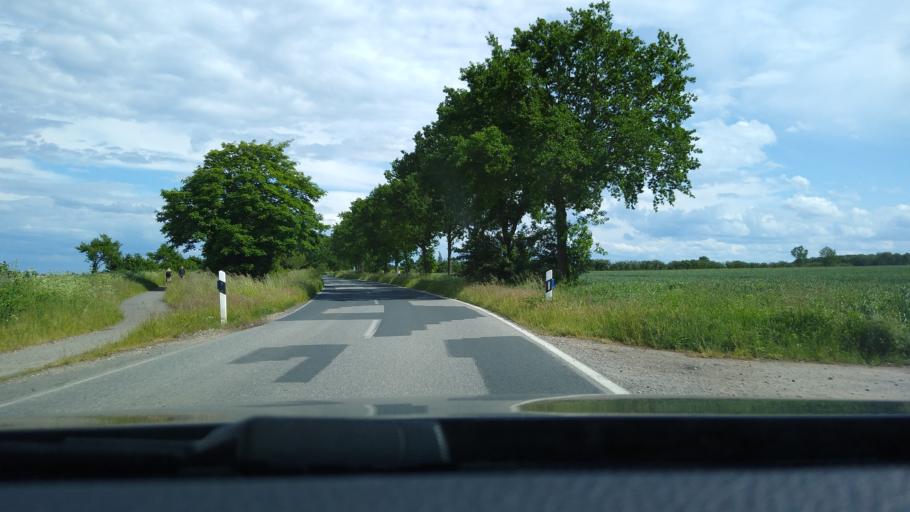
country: DE
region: Schleswig-Holstein
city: Dahme
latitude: 54.2271
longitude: 11.0645
